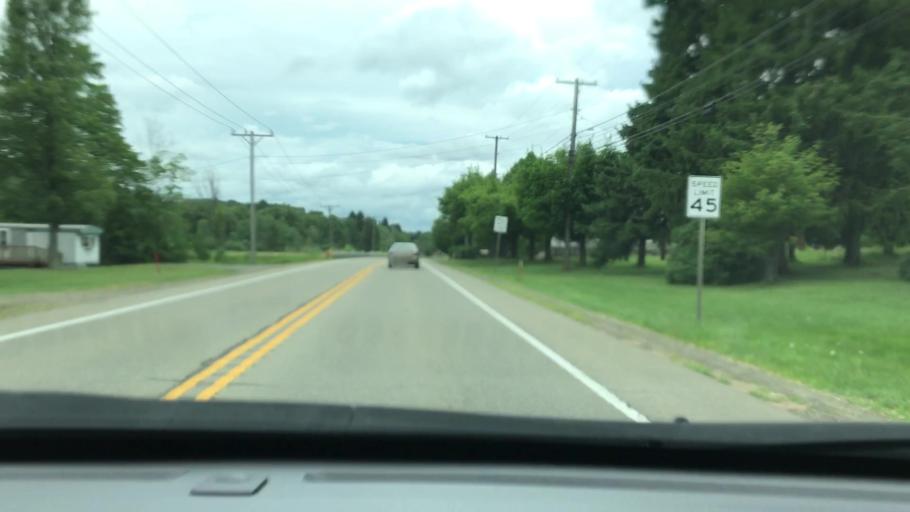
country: US
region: Pennsylvania
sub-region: Elk County
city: Johnsonburg
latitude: 41.5049
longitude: -78.6794
